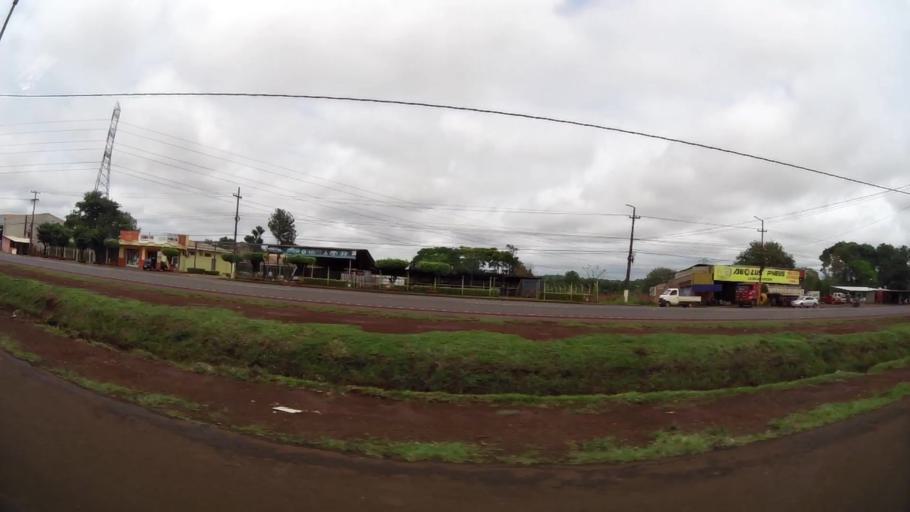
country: PY
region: Alto Parana
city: Ciudad del Este
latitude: -25.4957
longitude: -54.6891
